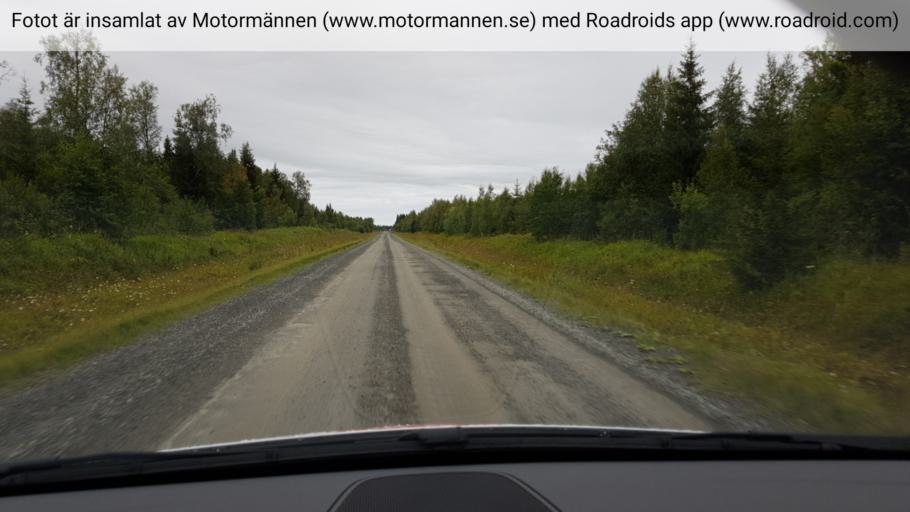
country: SE
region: Jaemtland
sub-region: OEstersunds Kommun
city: Lit
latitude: 63.6743
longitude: 14.8763
